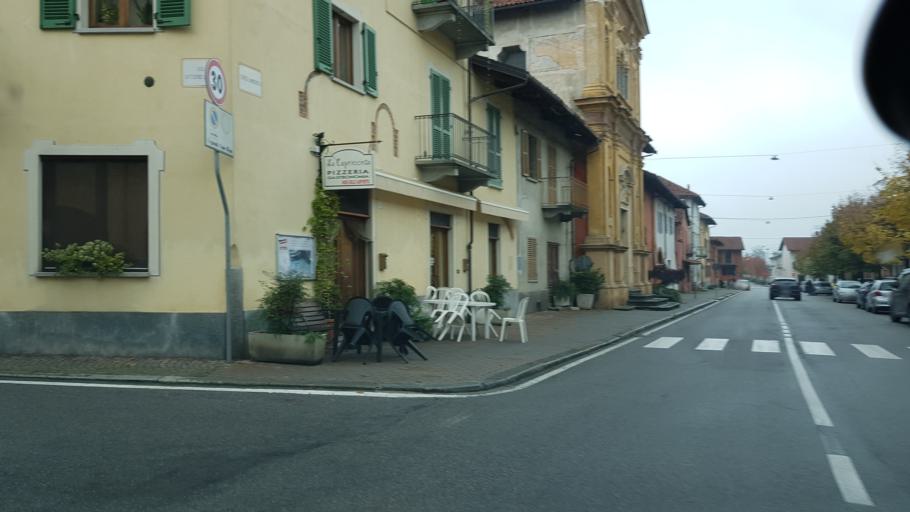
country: IT
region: Piedmont
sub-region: Provincia di Cuneo
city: Villafalletto
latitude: 44.5456
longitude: 7.5410
